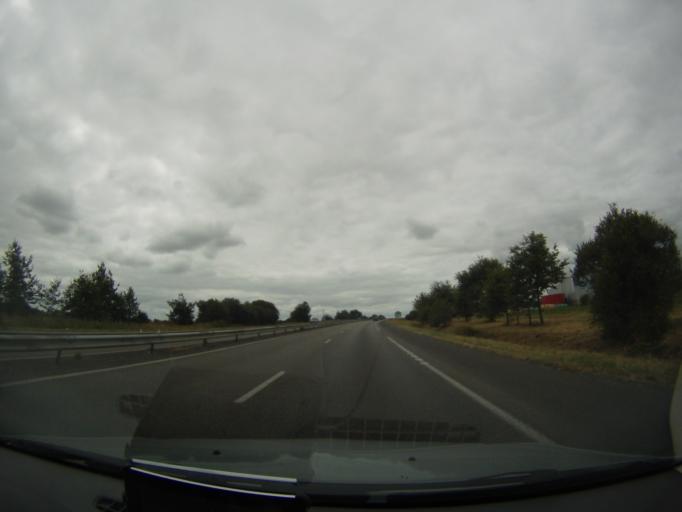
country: FR
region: Pays de la Loire
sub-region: Departement de la Loire-Atlantique
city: Heric
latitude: 47.3710
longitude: -1.6459
